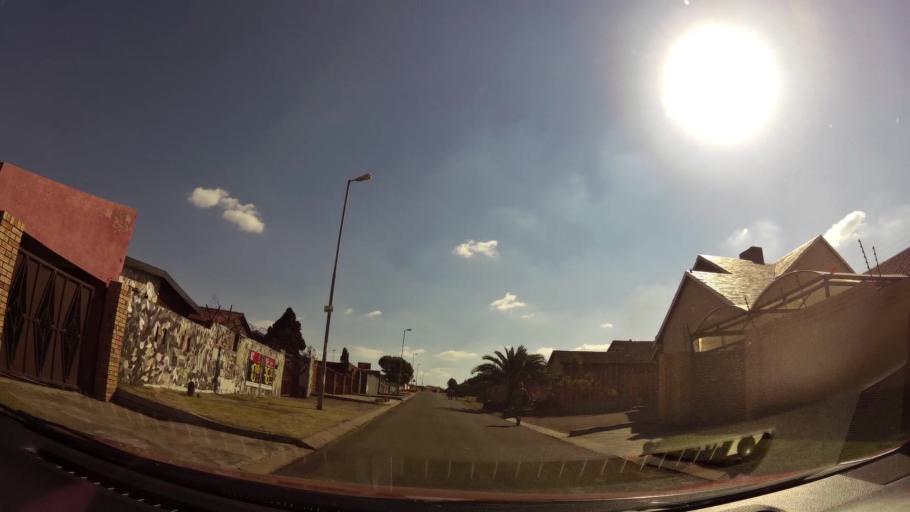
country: ZA
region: Gauteng
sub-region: City of Johannesburg Metropolitan Municipality
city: Soweto
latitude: -26.2396
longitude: 27.9039
